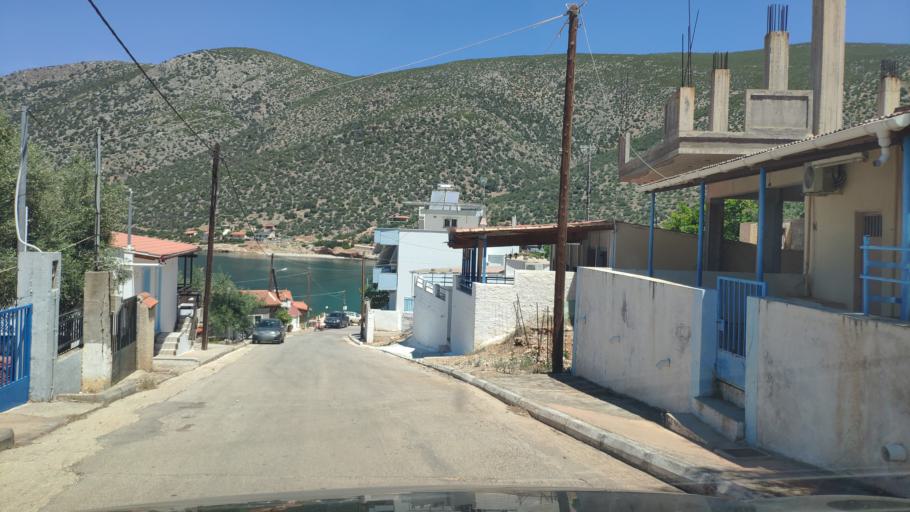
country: GR
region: Central Greece
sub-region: Nomos Voiotias
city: Kaparellion
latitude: 38.1795
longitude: 23.1423
